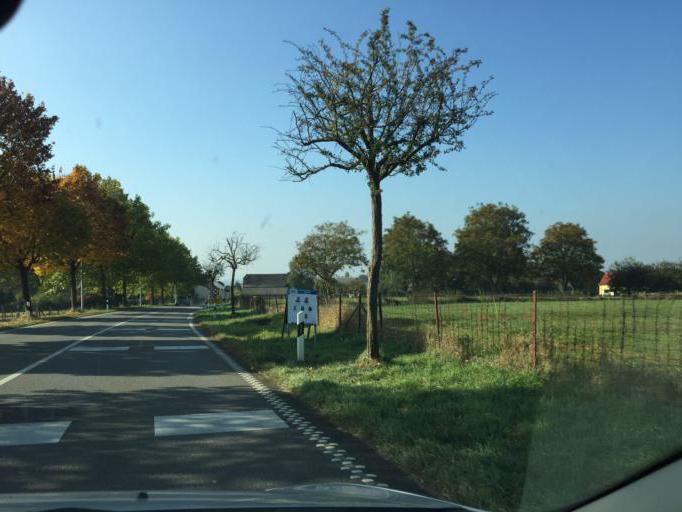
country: LU
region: Grevenmacher
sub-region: Canton de Remich
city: Dalheim
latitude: 49.5366
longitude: 6.2513
